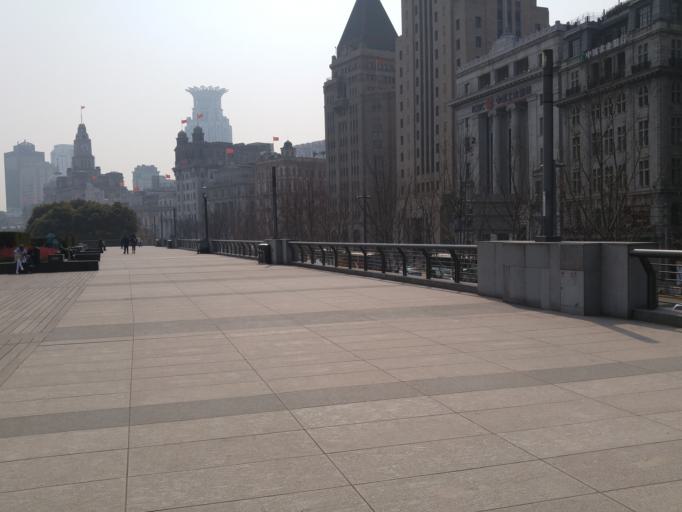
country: CN
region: Shanghai Shi
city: Hongkou
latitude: 31.2425
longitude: 121.4861
